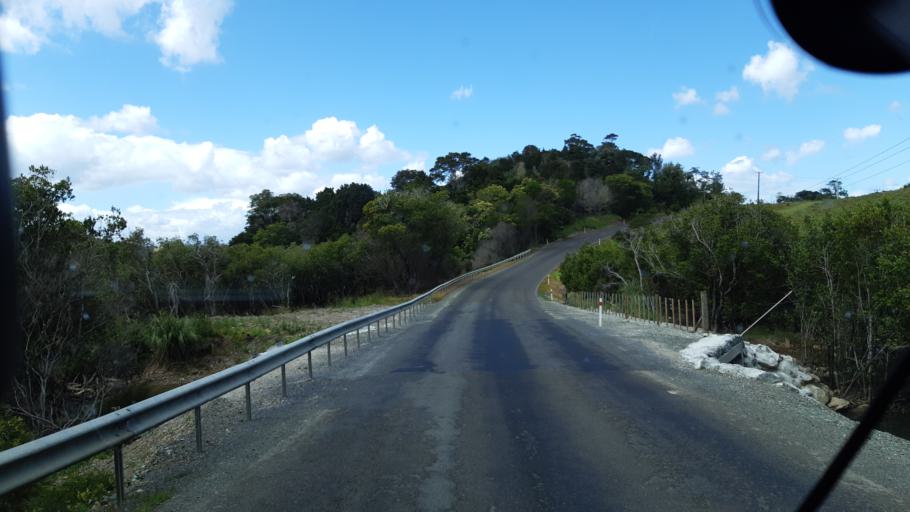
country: NZ
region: Northland
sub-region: Far North District
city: Taipa
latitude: -35.2669
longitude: 173.5248
